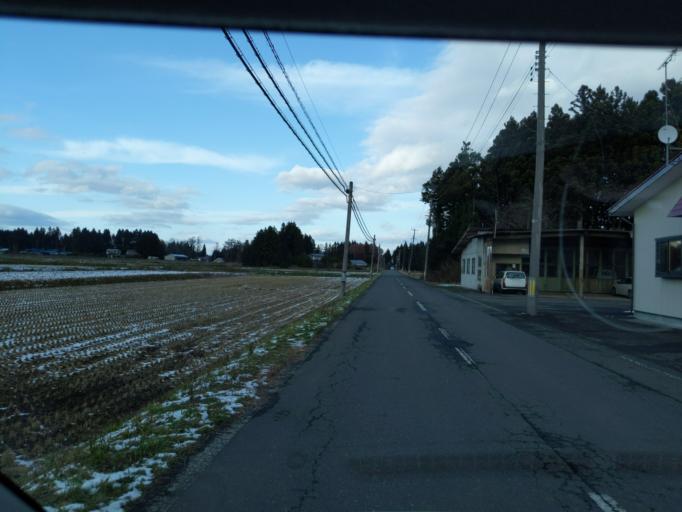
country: JP
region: Iwate
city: Kitakami
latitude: 39.2066
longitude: 141.0477
